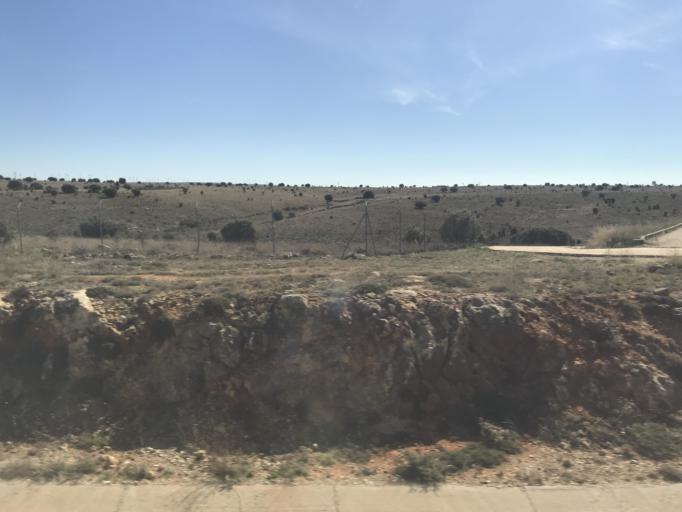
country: ES
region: Castille-La Mancha
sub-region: Provincia de Guadalajara
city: Anguita
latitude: 41.1207
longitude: -2.3491
